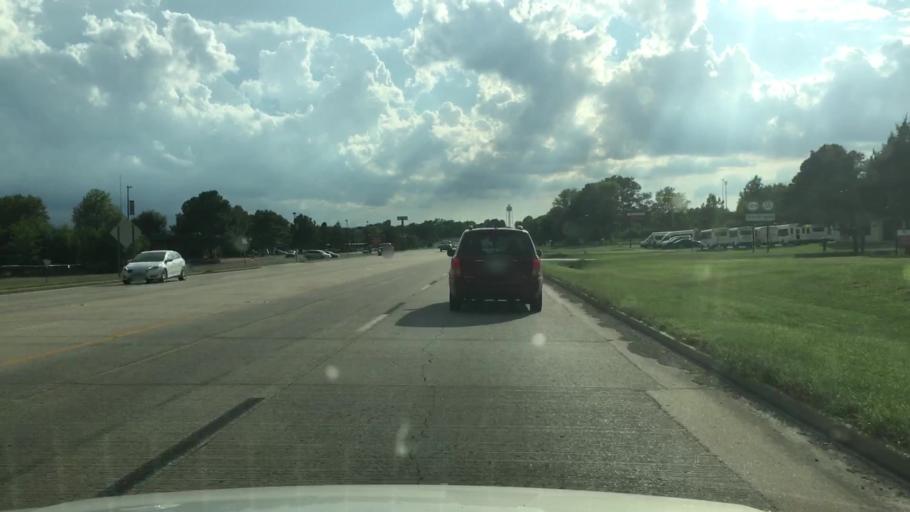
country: US
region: Oklahoma
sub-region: Cherokee County
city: Park Hill
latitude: 35.8551
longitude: -94.9863
